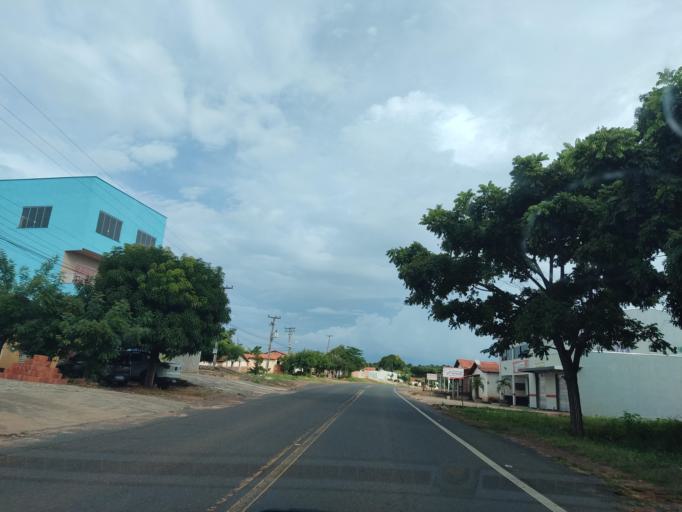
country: BR
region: Piaui
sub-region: Agua Branca
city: Agua Branca
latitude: -5.8212
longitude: -42.5080
